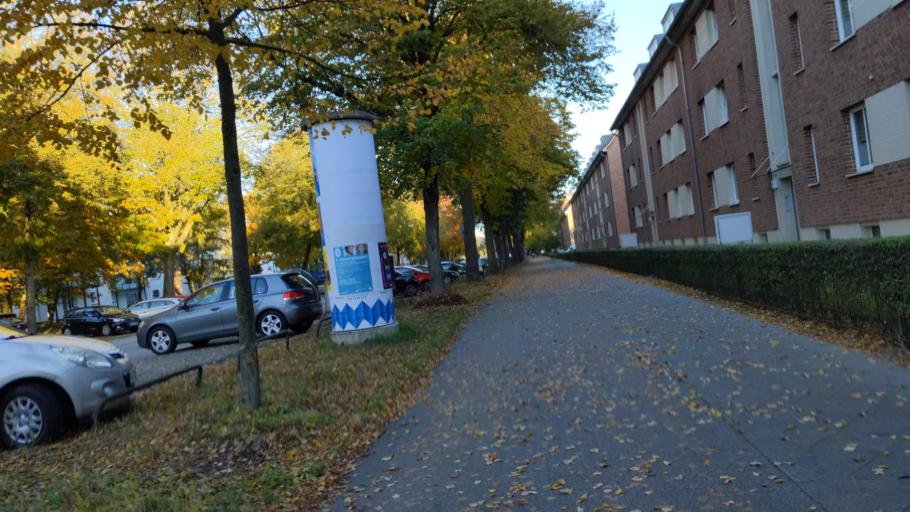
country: DE
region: Schleswig-Holstein
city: Luebeck
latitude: 53.8647
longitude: 10.7246
